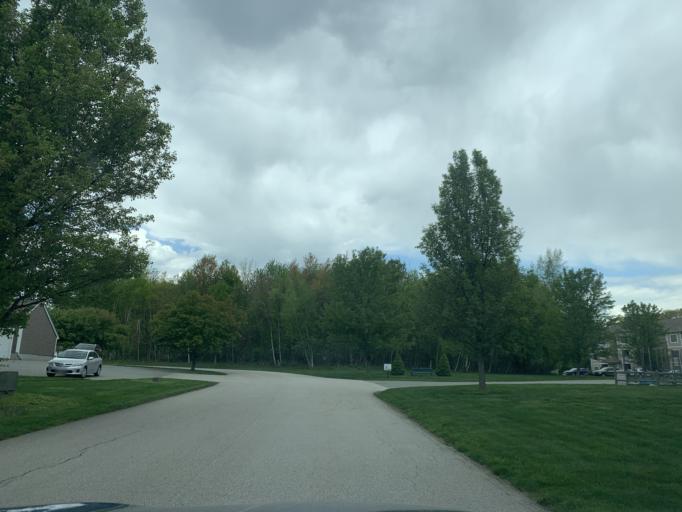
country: US
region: Rhode Island
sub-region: Kent County
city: East Greenwich
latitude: 41.6714
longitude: -71.4919
